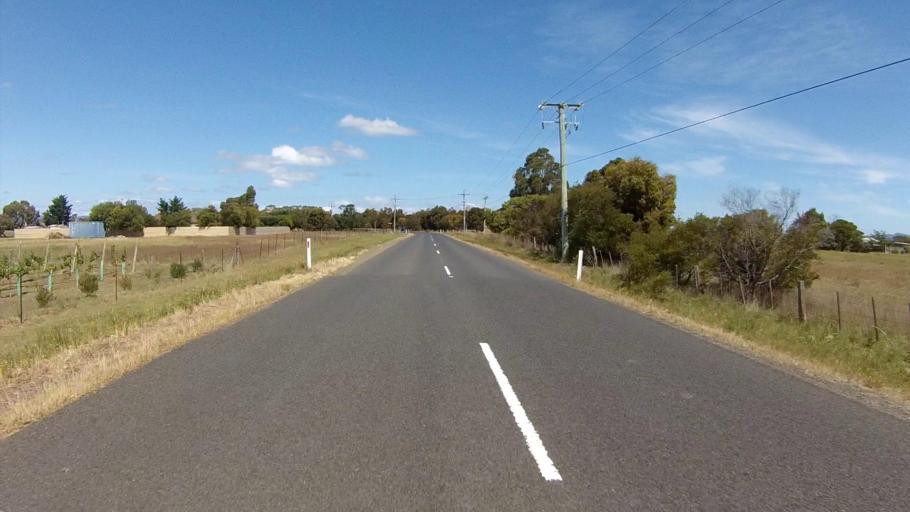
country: AU
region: Tasmania
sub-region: Sorell
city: Sorell
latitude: -42.7779
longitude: 147.5213
